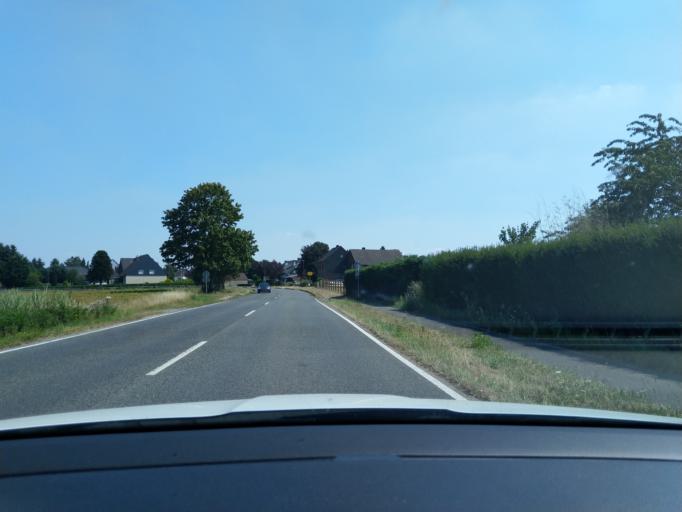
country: DE
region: North Rhine-Westphalia
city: Wegberg
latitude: 51.1363
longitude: 6.2366
